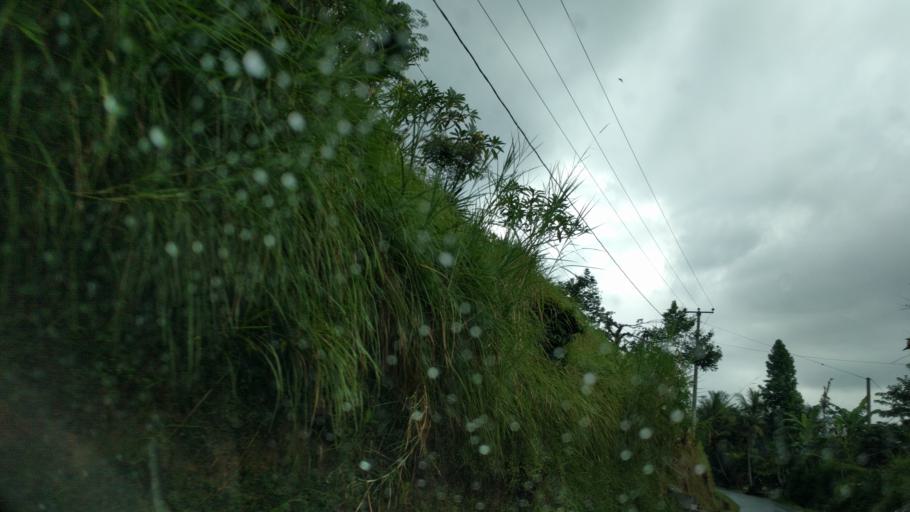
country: ID
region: Bali
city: Bunutan
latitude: -8.4721
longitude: 115.2600
